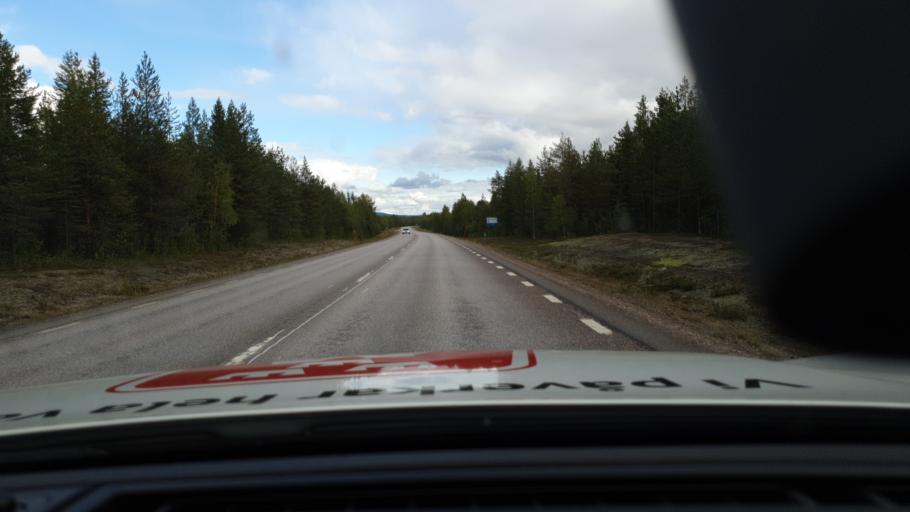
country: SE
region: Norrbotten
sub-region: Gallivare Kommun
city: Gaellivare
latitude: 67.1047
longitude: 20.8693
